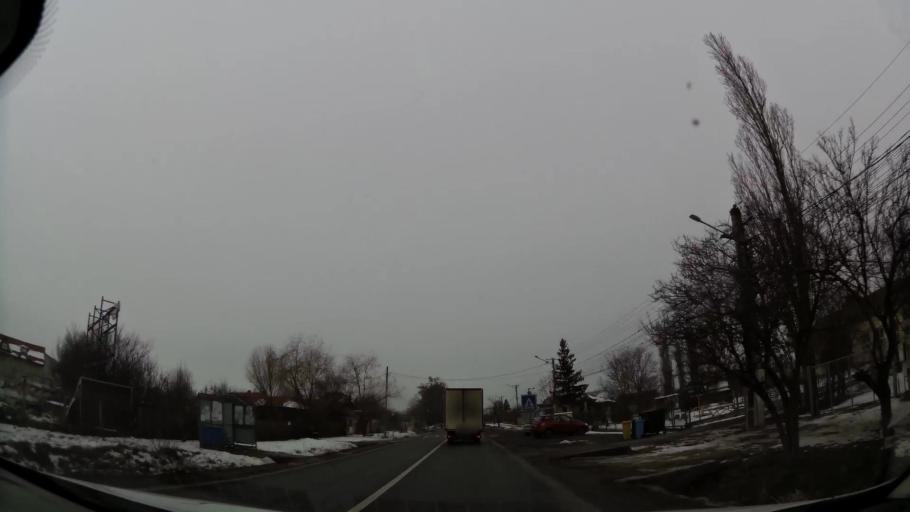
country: RO
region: Dambovita
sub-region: Comuna Tartasesti
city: Baldana
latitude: 44.6027
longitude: 25.7767
